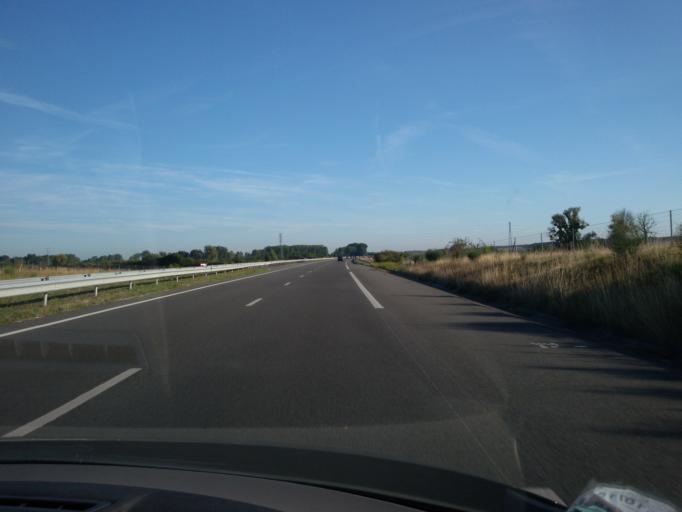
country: FR
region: Centre
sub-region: Departement du Cher
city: Orval
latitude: 46.8043
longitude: 2.4128
